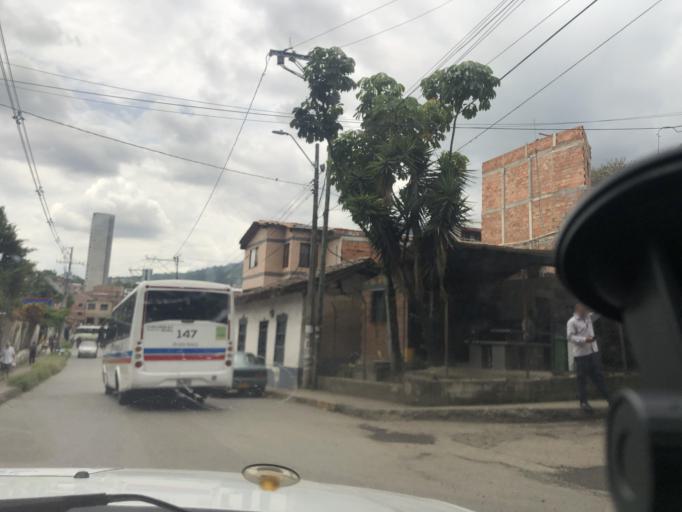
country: CO
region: Antioquia
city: Bello
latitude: 6.3460
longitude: -75.5642
